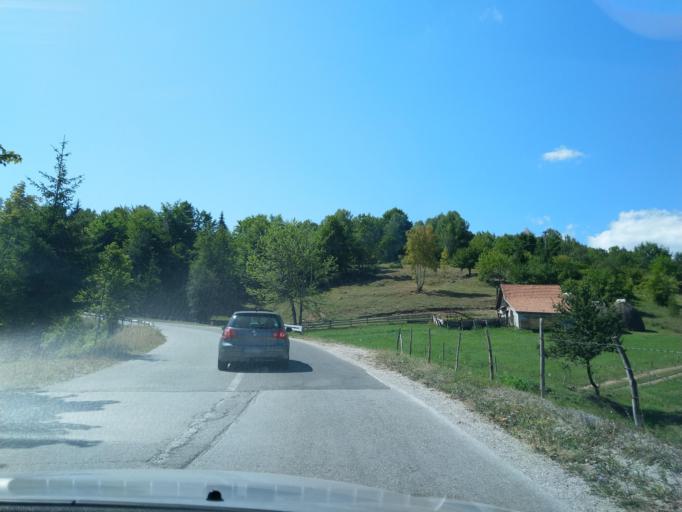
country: RS
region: Central Serbia
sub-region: Zlatiborski Okrug
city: Nova Varos
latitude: 43.4195
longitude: 19.8282
